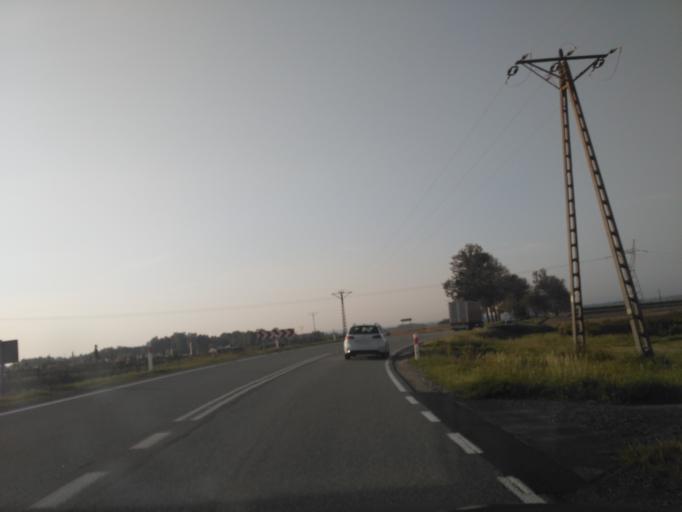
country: PL
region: Lublin Voivodeship
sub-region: Powiat krasnicki
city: Szastarka
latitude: 50.8164
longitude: 22.3188
